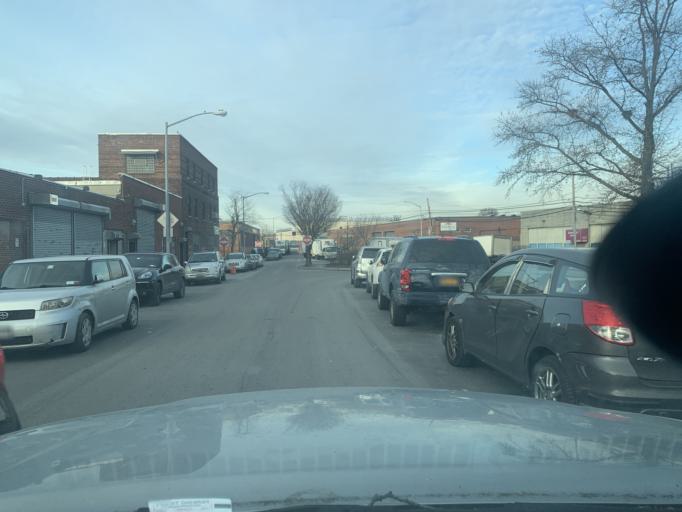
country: US
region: New York
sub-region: Queens County
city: Long Island City
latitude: 40.7360
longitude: -73.8905
